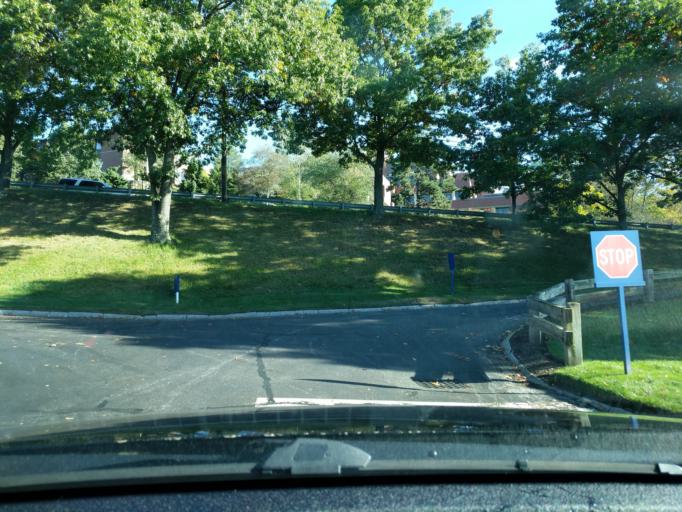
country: US
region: Massachusetts
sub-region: Middlesex County
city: Lexington
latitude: 42.4242
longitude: -71.2488
